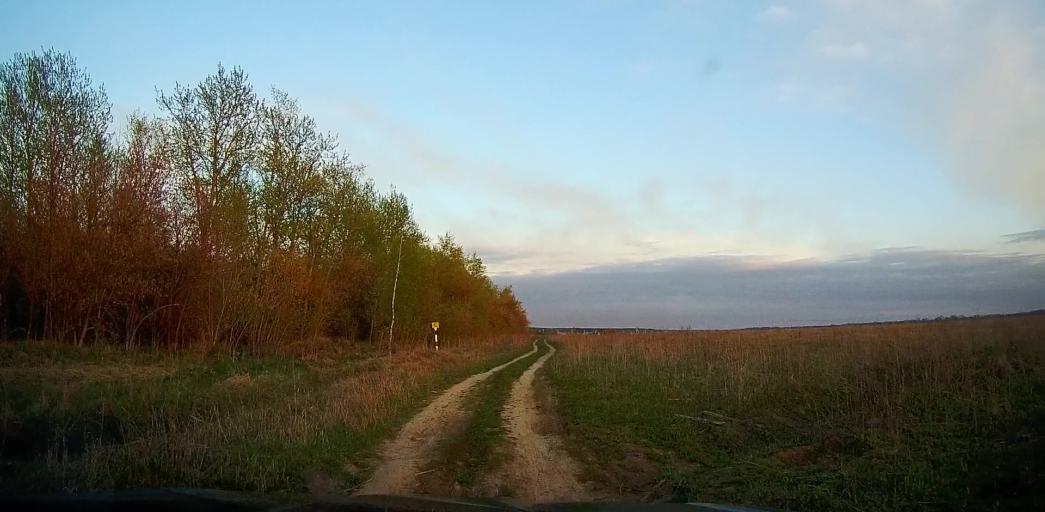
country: RU
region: Moskovskaya
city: Peski
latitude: 55.2337
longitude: 38.7291
